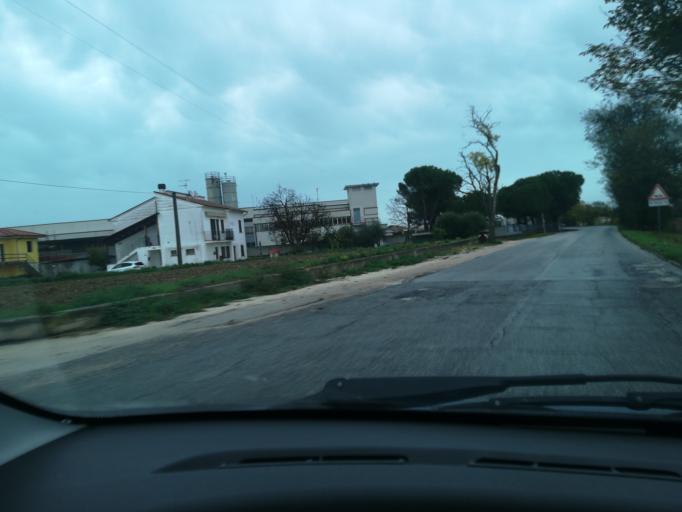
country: IT
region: The Marches
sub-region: Provincia di Macerata
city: Trodica
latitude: 43.2765
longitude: 13.6036
